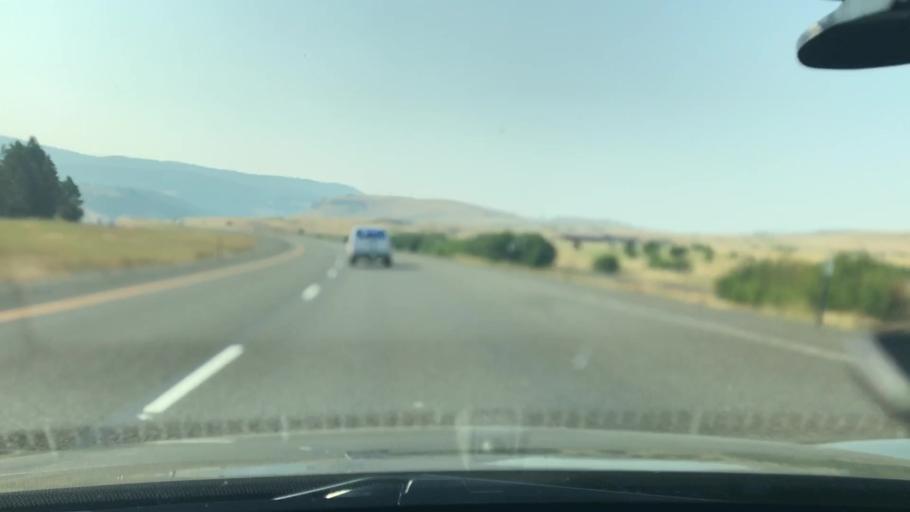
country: US
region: Oregon
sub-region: Union County
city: Union
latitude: 45.1863
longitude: -117.9905
